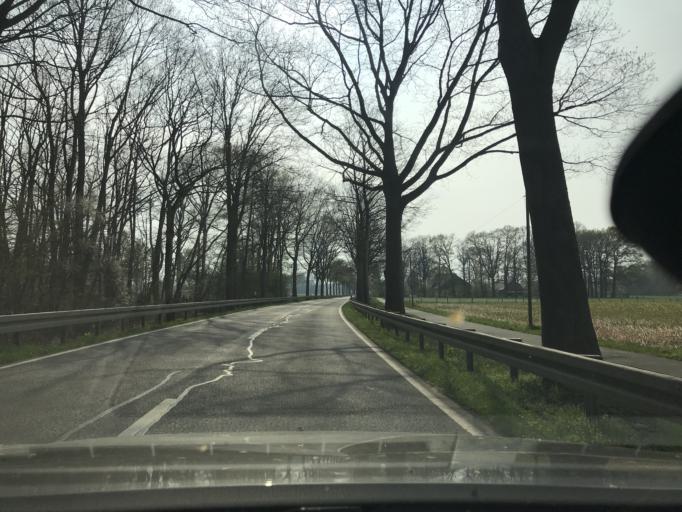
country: DE
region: North Rhine-Westphalia
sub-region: Regierungsbezirk Dusseldorf
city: Wachtendonk
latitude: 51.4559
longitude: 6.3381
